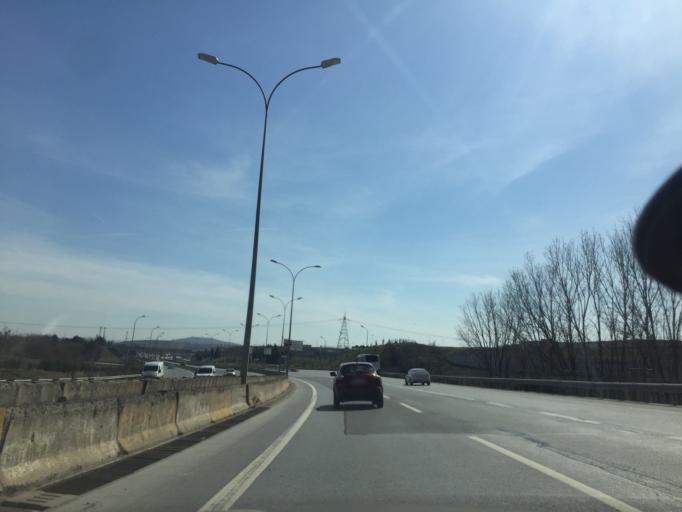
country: TR
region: Istanbul
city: Pendik
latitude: 40.9190
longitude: 29.3216
